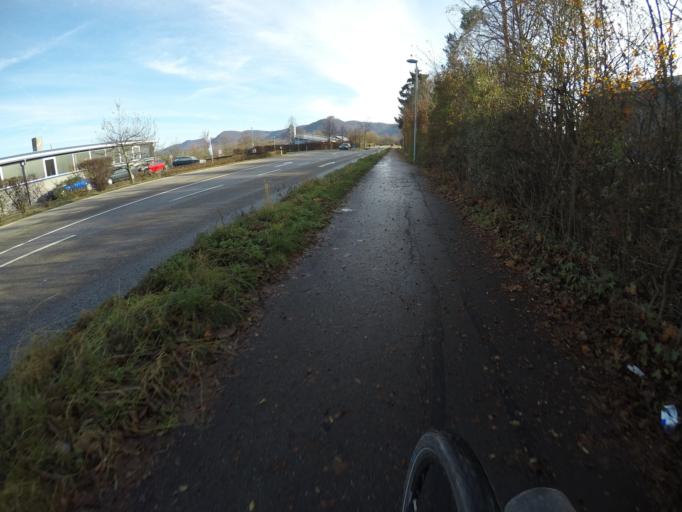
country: DE
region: Baden-Wuerttemberg
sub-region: Regierungsbezirk Stuttgart
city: Kohlberg
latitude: 48.5595
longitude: 9.3449
